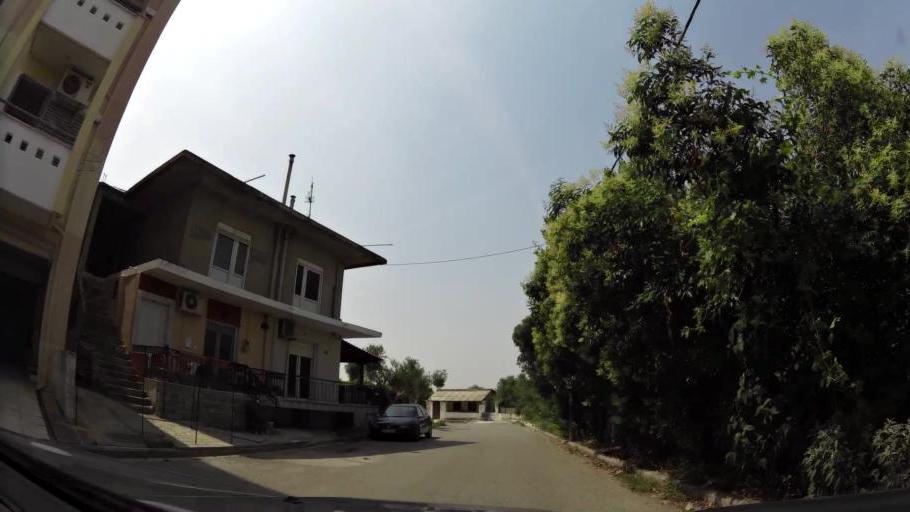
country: GR
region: Central Macedonia
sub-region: Nomos Thessalonikis
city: Diavata
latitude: 40.6917
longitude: 22.8572
